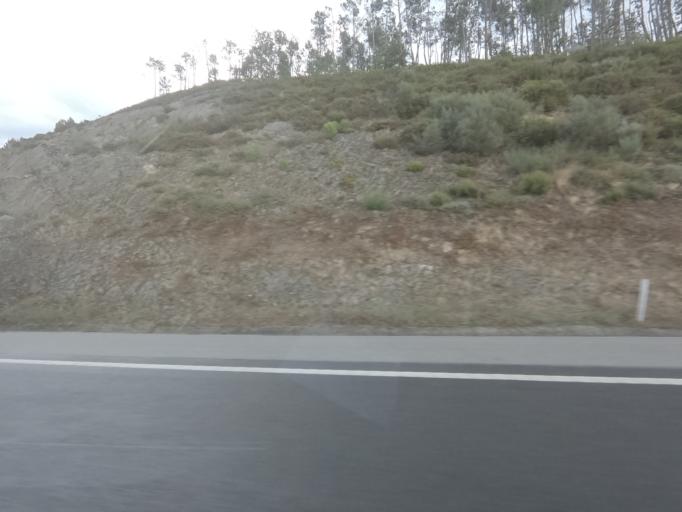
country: PT
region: Viseu
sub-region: Lamego
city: Lamego
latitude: 41.0477
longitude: -7.8594
